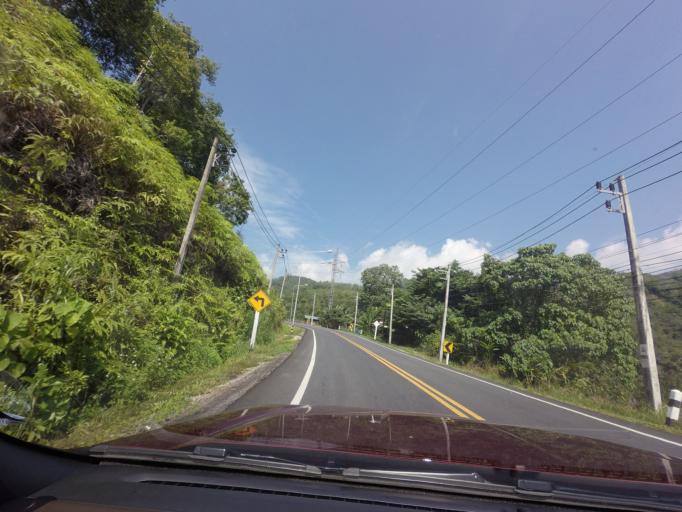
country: TH
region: Yala
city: Betong
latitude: 5.9074
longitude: 101.1492
